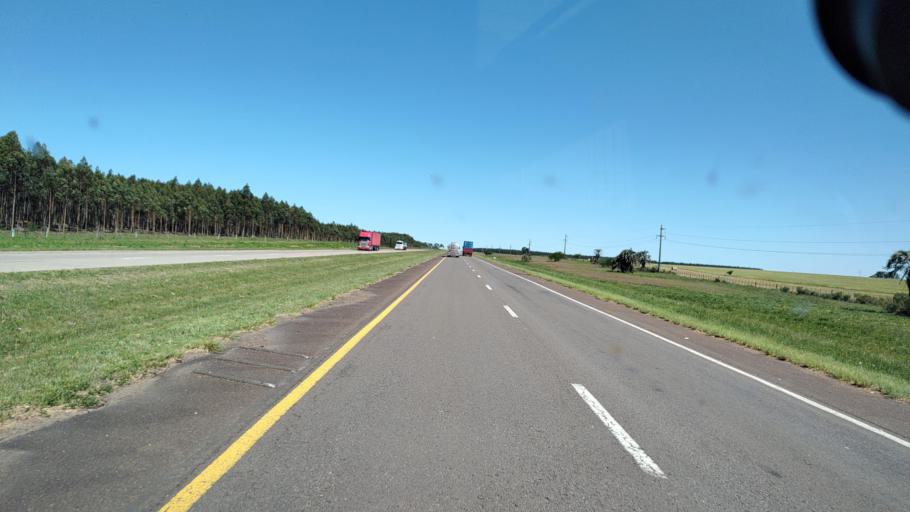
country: AR
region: Entre Rios
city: Villa Elisa
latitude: -32.0199
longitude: -58.2842
